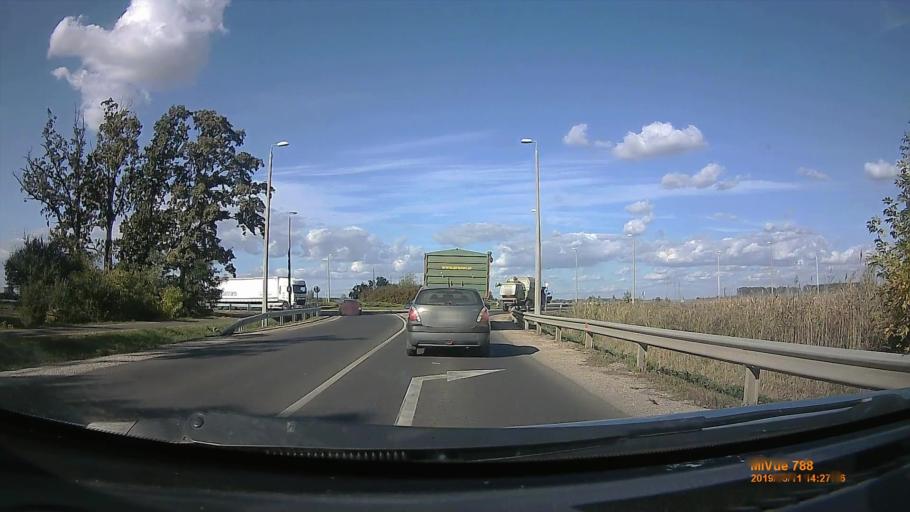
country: HU
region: Hajdu-Bihar
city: Balmazujvaros
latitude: 47.5550
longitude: 21.3575
